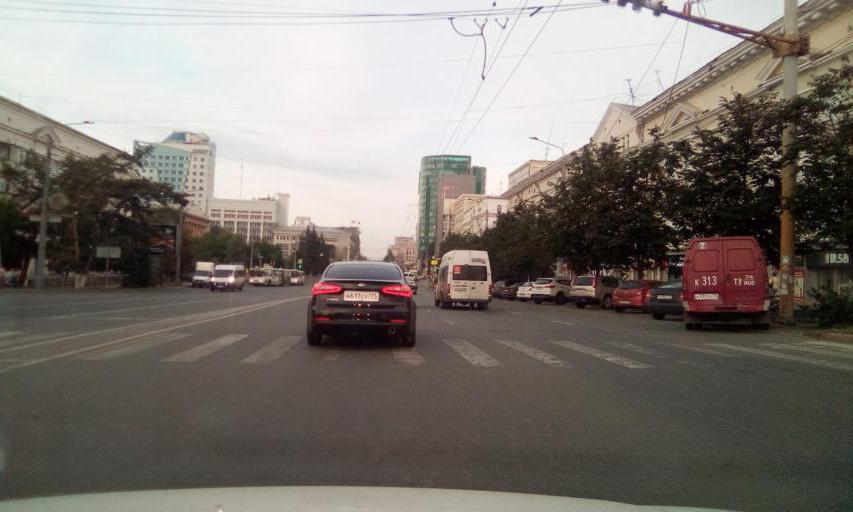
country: RU
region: Chelyabinsk
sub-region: Gorod Chelyabinsk
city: Chelyabinsk
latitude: 55.1600
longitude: 61.3938
